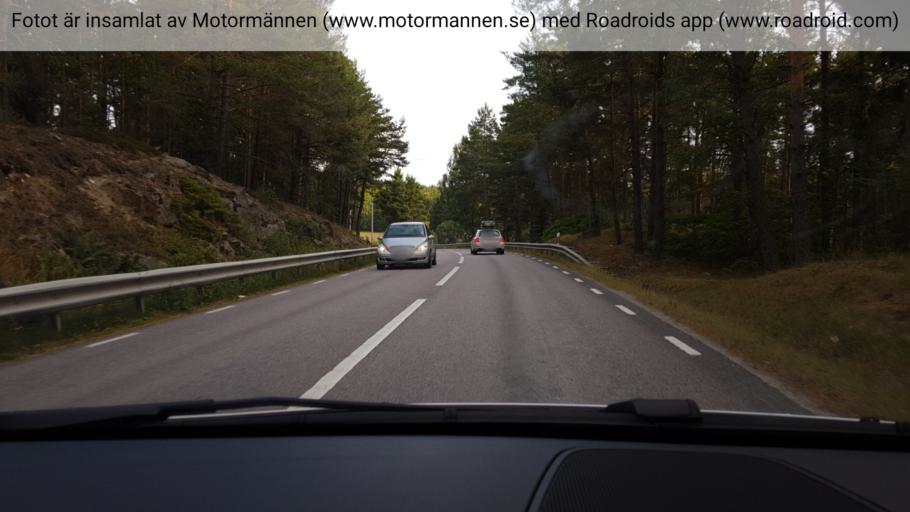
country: SE
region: Stockholm
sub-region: Sigtuna Kommun
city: Sigtuna
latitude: 59.6385
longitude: 17.7060
